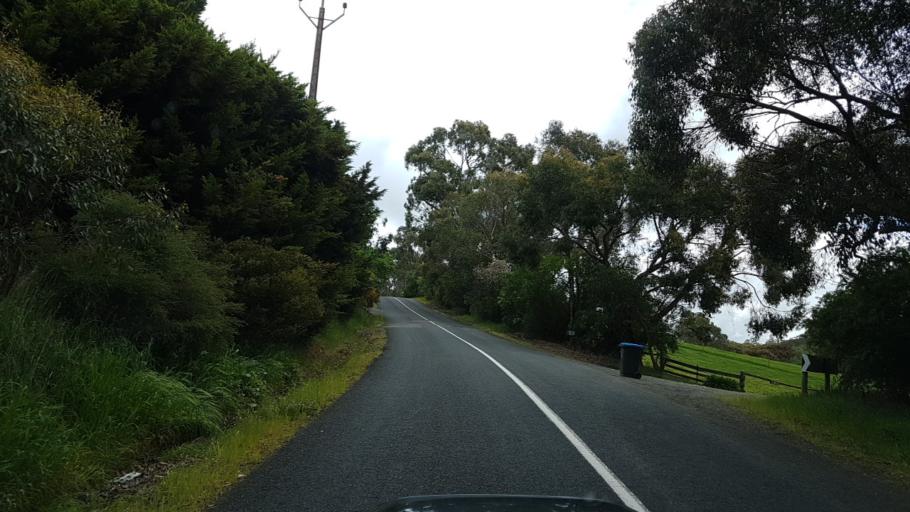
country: AU
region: South Australia
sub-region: Adelaide Hills
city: Lobethal
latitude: -34.8902
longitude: 138.8917
